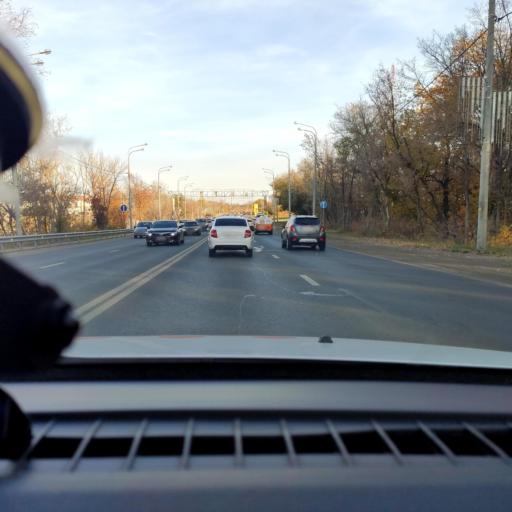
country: RU
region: Samara
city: Samara
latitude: 53.2854
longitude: 50.2266
